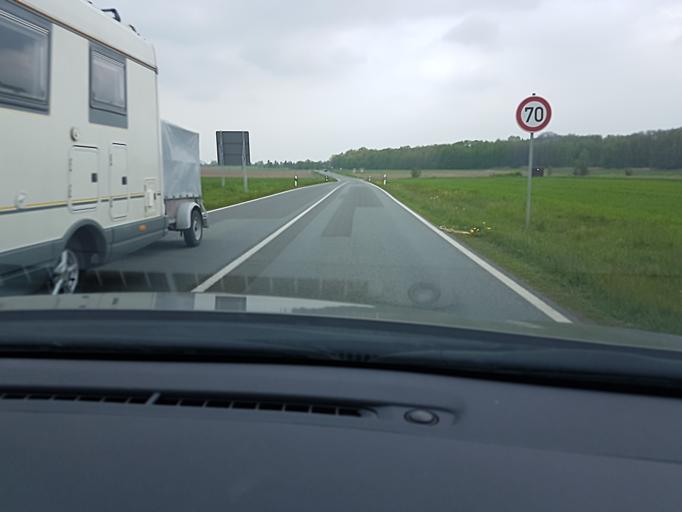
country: DE
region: Saxony
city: Belgern
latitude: 51.4630
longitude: 13.1543
